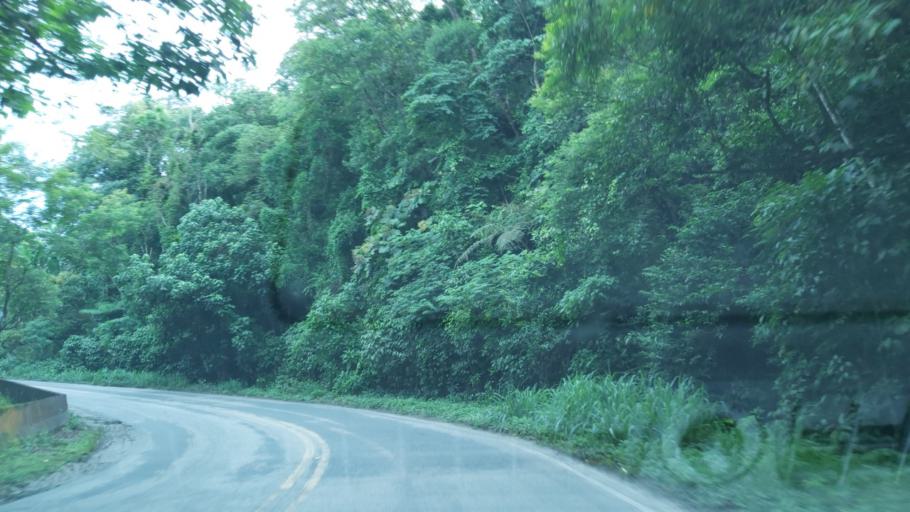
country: BR
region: Sao Paulo
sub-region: Miracatu
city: Miracatu
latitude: -24.0510
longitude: -47.5708
